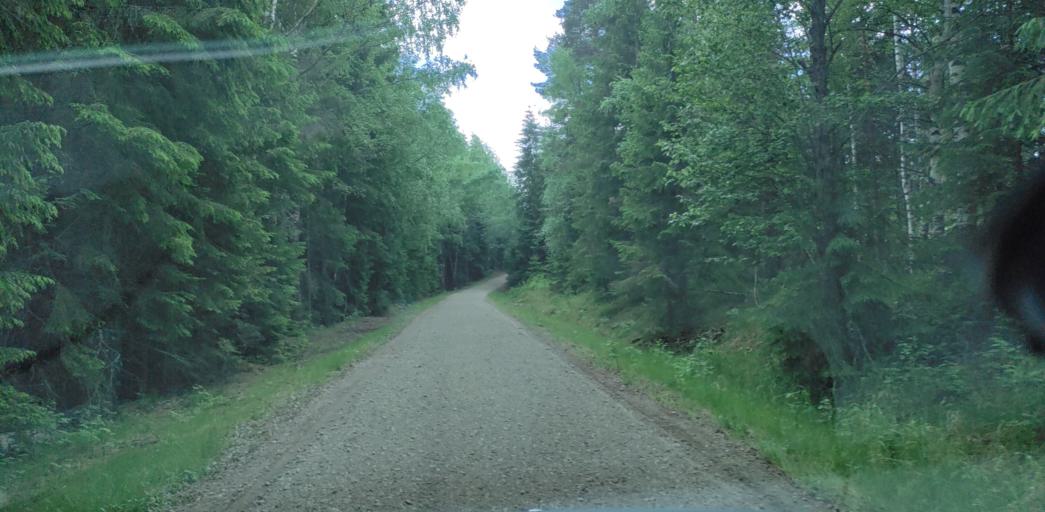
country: SE
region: Vaermland
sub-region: Munkfors Kommun
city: Munkfors
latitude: 59.9675
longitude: 13.4207
